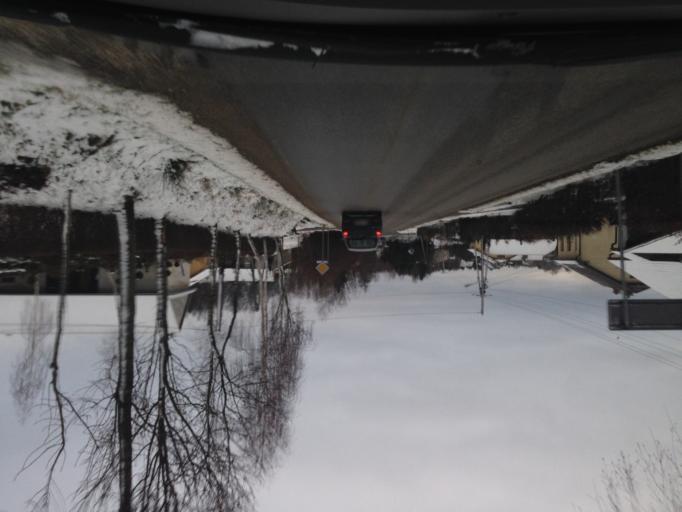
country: PL
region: Lesser Poland Voivodeship
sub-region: Powiat gorlicki
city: Moszczenica
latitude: 49.7420
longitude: 21.0833
